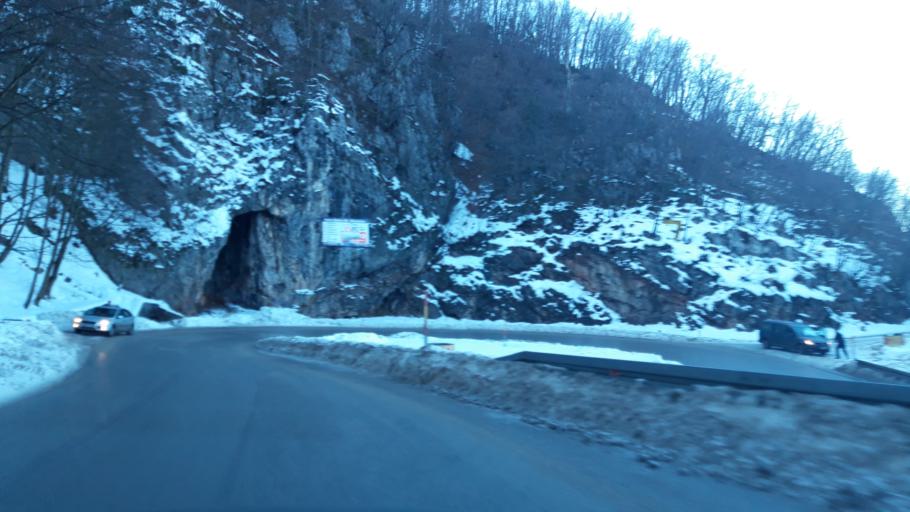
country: BA
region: Republika Srpska
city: Vlasenica
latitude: 44.1589
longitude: 18.9259
